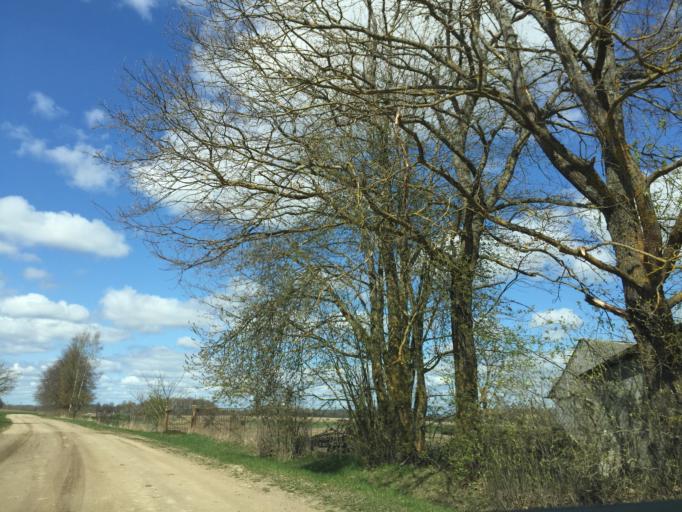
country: LV
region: Vilanu
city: Vilani
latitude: 56.6579
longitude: 27.1214
